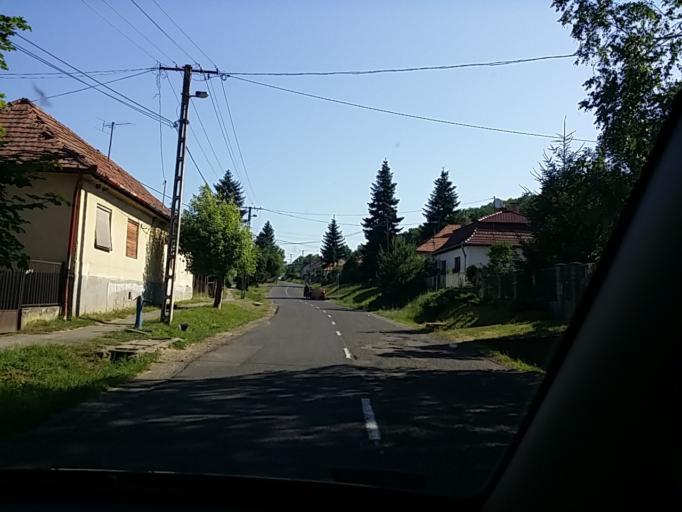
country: HU
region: Nograd
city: Karancskeszi
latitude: 48.2123
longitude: 19.5982
